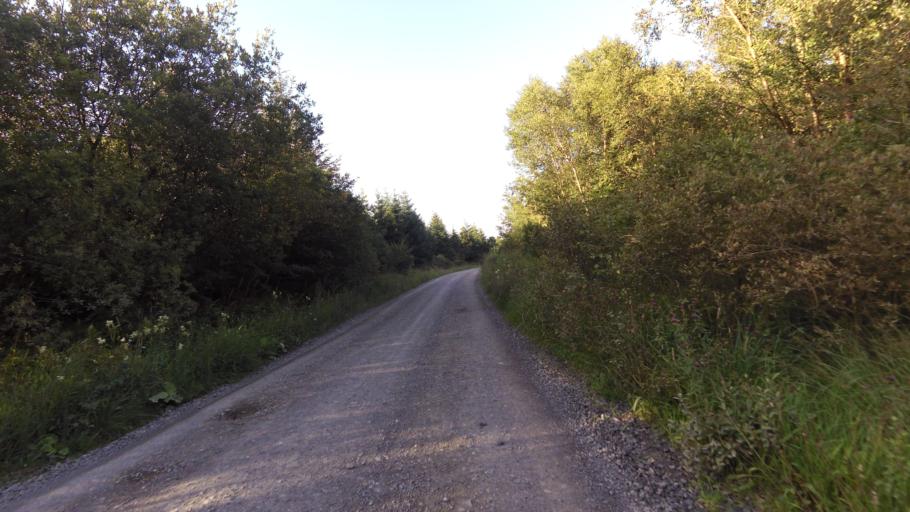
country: GB
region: England
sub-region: Lancashire
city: Clitheroe
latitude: 53.9944
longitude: -2.3926
